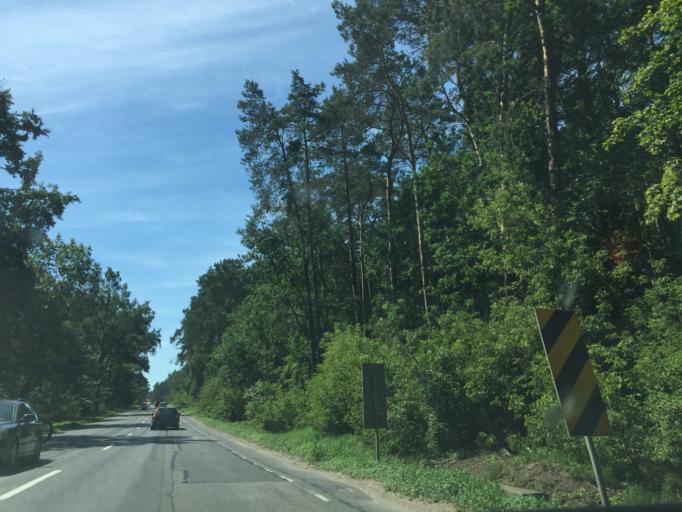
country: PL
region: Lodz Voivodeship
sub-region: Piotrkow Trybunalski
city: Piotrkow Trybunalski
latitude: 51.4334
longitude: 19.7181
